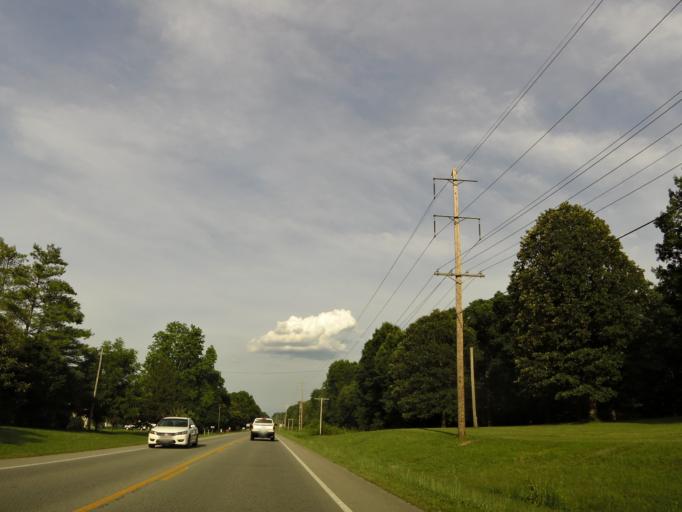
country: US
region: Tennessee
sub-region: Dickson County
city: Dickson
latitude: 36.0900
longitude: -87.4891
